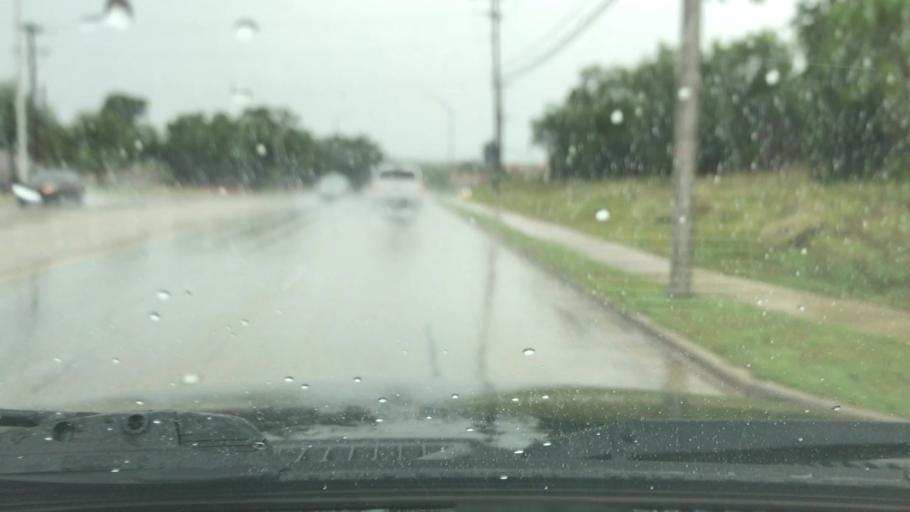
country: US
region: Texas
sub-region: Williamson County
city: Cedar Park
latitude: 30.4983
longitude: -97.8198
